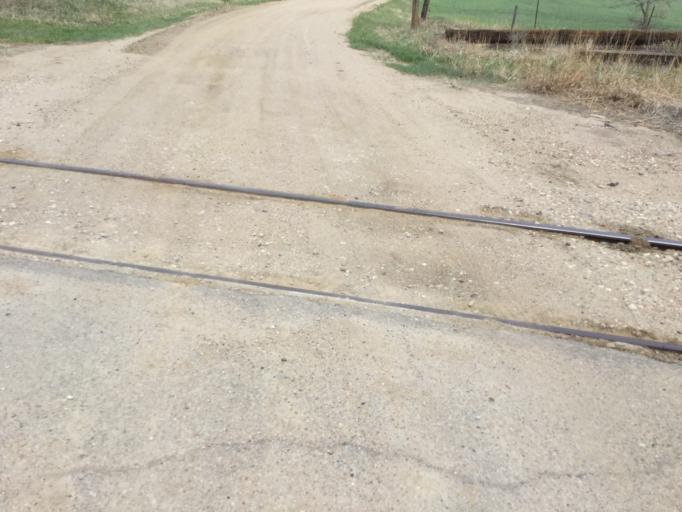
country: US
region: Kansas
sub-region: Norton County
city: Norton
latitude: 39.7675
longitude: -100.0764
